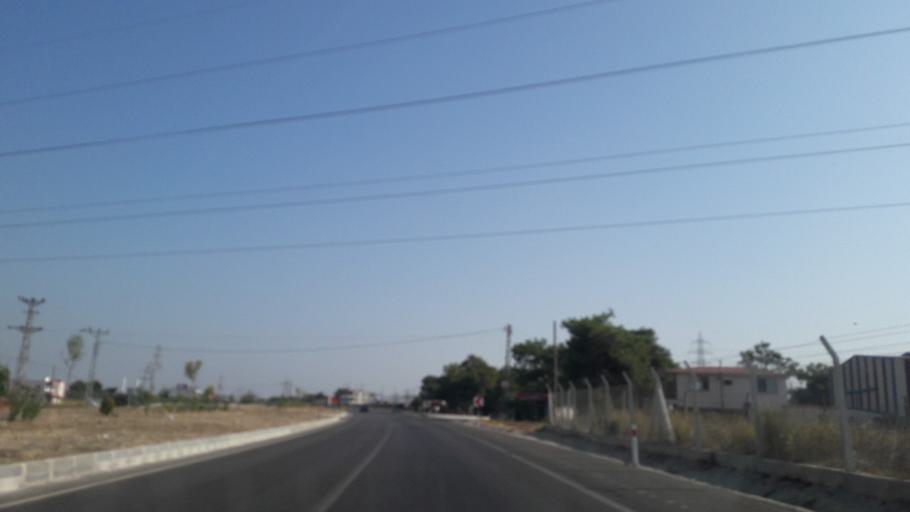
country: TR
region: Adana
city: Yakapinar
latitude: 37.1005
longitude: 35.5062
